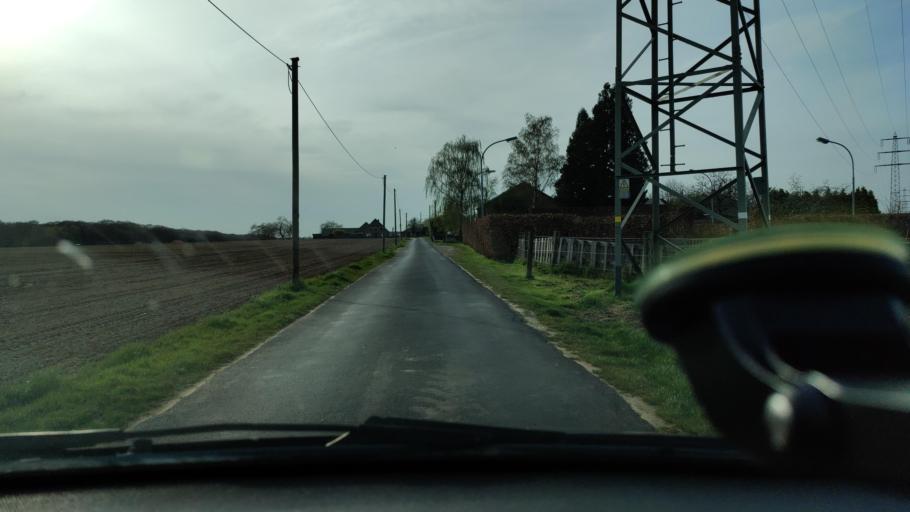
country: DE
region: North Rhine-Westphalia
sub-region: Regierungsbezirk Dusseldorf
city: Goch
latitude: 51.7406
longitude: 6.1896
